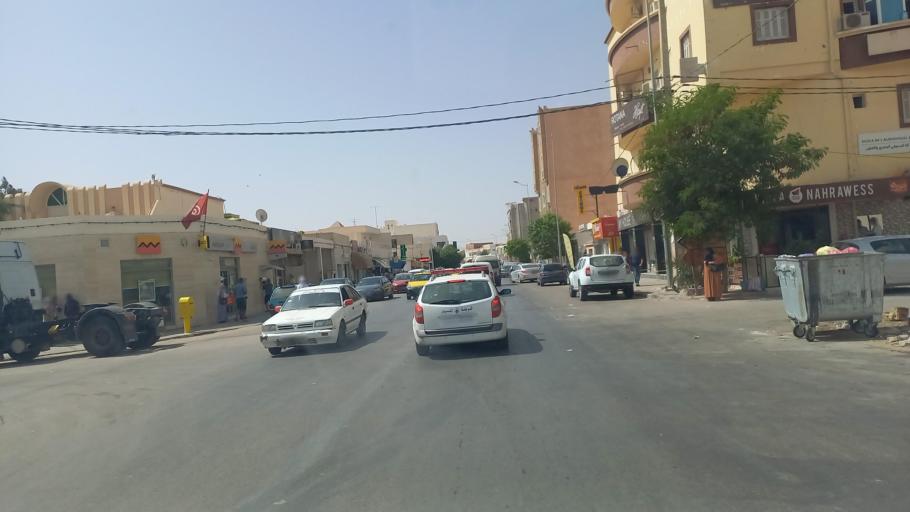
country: TN
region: Madanin
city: Medenine
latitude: 33.3387
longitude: 10.4868
